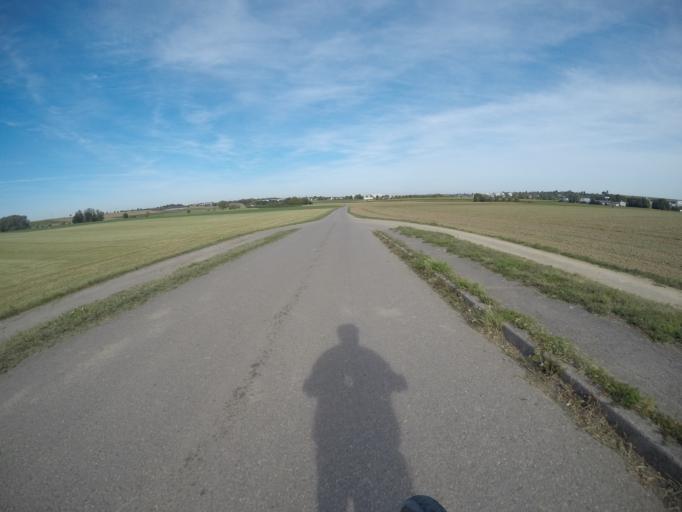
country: DE
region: Baden-Wuerttemberg
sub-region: Regierungsbezirk Stuttgart
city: Korntal
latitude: 48.8435
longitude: 9.1086
